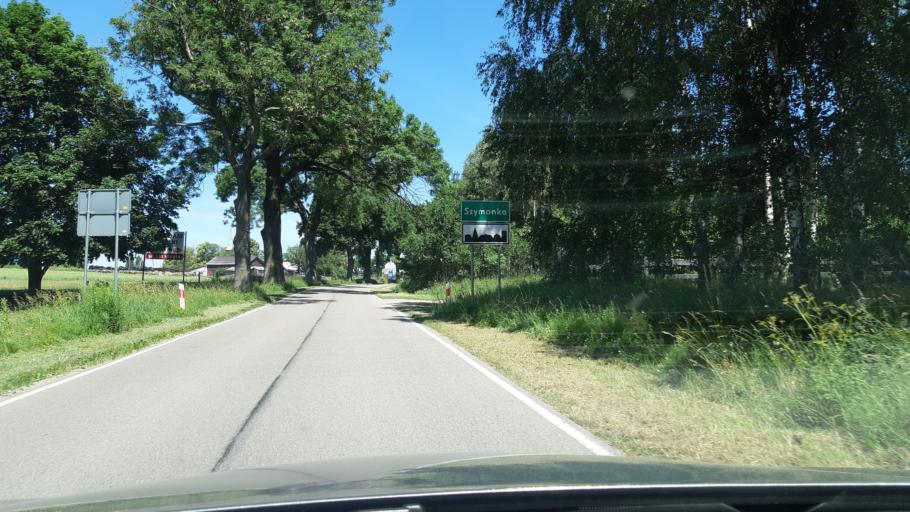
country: PL
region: Warmian-Masurian Voivodeship
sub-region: Powiat gizycki
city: Ryn
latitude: 53.8904
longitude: 21.6586
